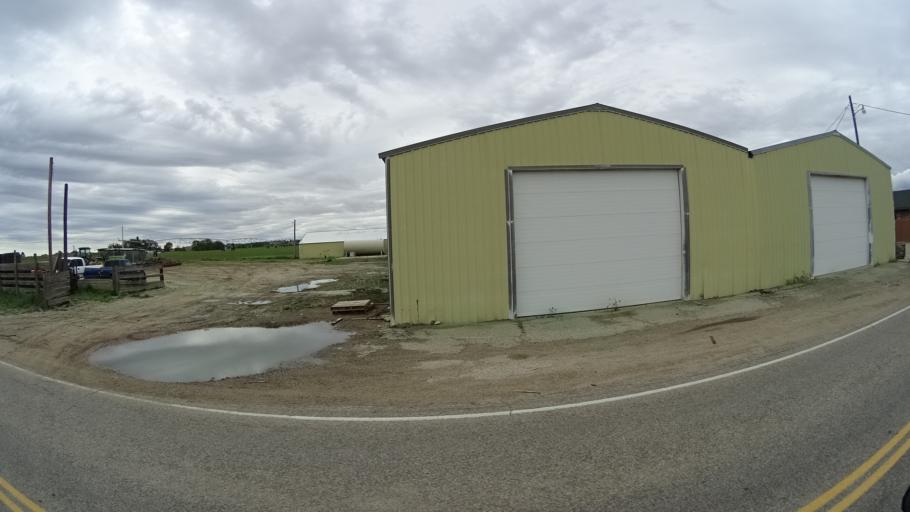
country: US
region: Idaho
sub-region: Ada County
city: Star
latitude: 43.7100
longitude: -116.4601
